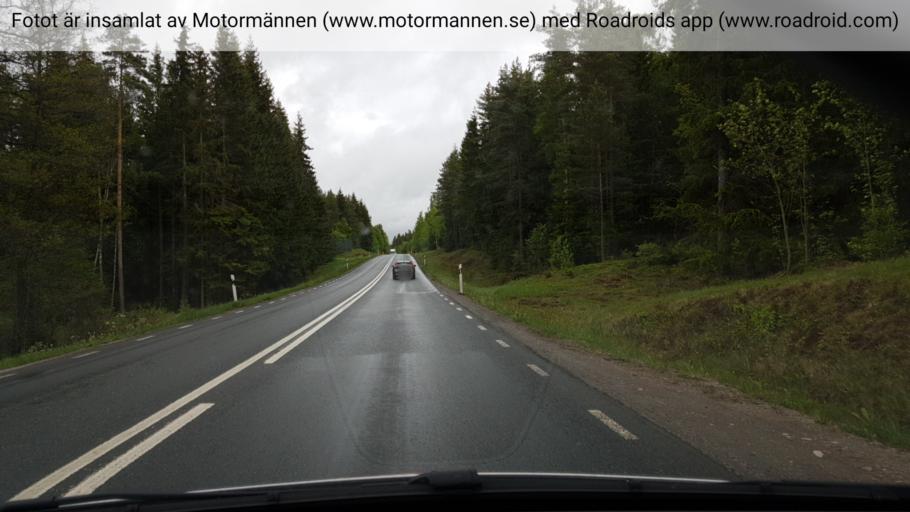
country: SE
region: Joenkoeping
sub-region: Aneby Kommun
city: Aneby
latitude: 57.8898
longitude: 14.8818
